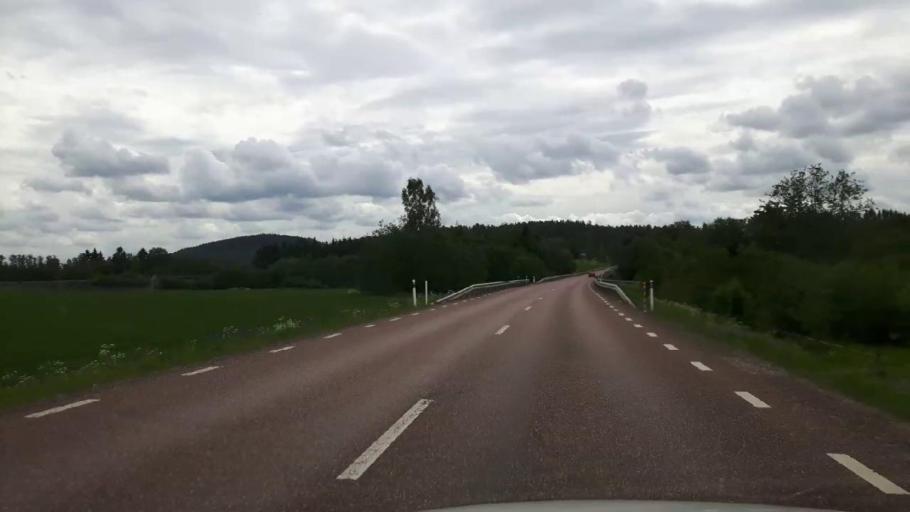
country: SE
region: Dalarna
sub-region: Hedemora Kommun
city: Brunna
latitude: 60.2319
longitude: 16.0005
